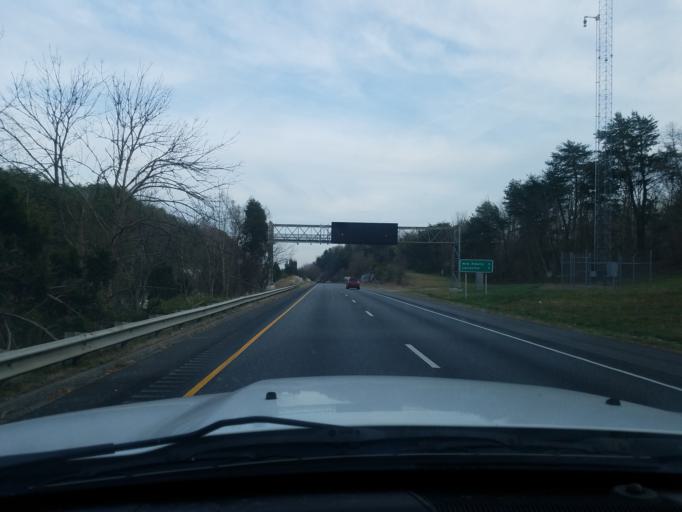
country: US
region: Indiana
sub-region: Floyd County
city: New Albany
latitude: 38.3029
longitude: -85.8764
